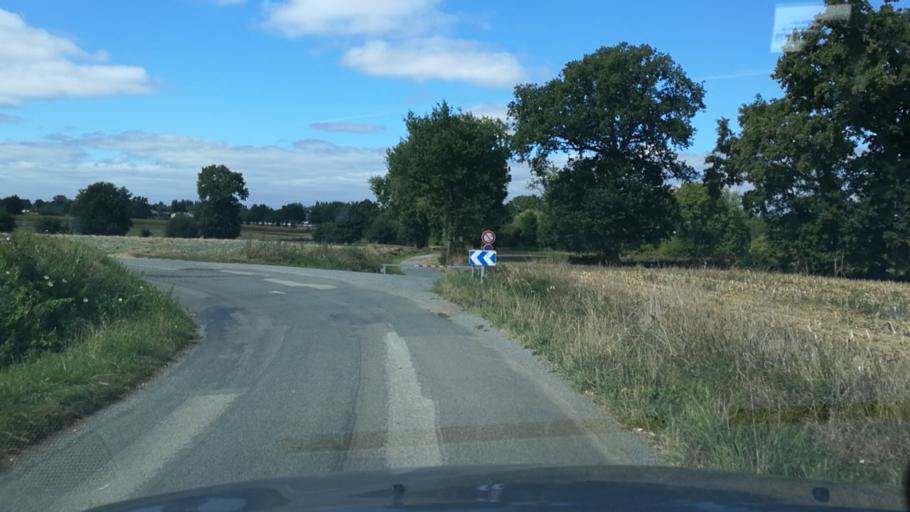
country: FR
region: Brittany
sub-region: Departement d'Ille-et-Vilaine
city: Montgermont
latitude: 48.1464
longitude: -1.7104
